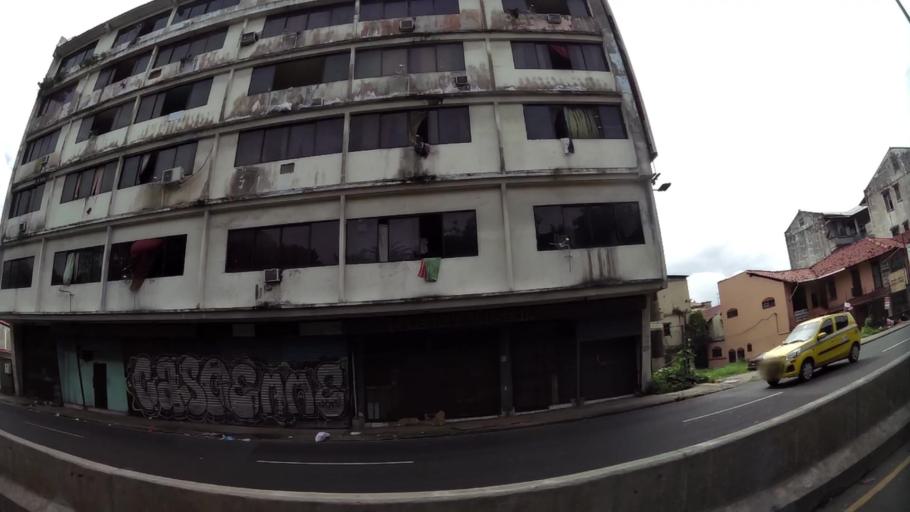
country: PA
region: Panama
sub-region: Distrito de Panama
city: Ancon
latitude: 8.9566
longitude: -79.5447
